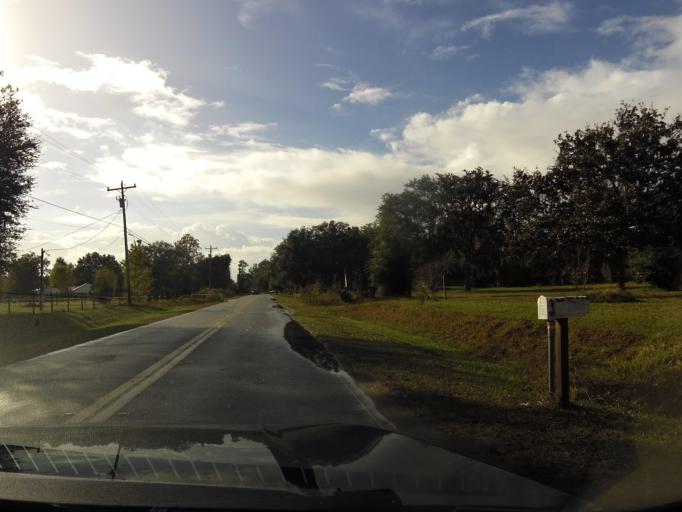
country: US
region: Florida
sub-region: Clay County
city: Asbury Lake
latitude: 30.0119
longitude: -81.8443
